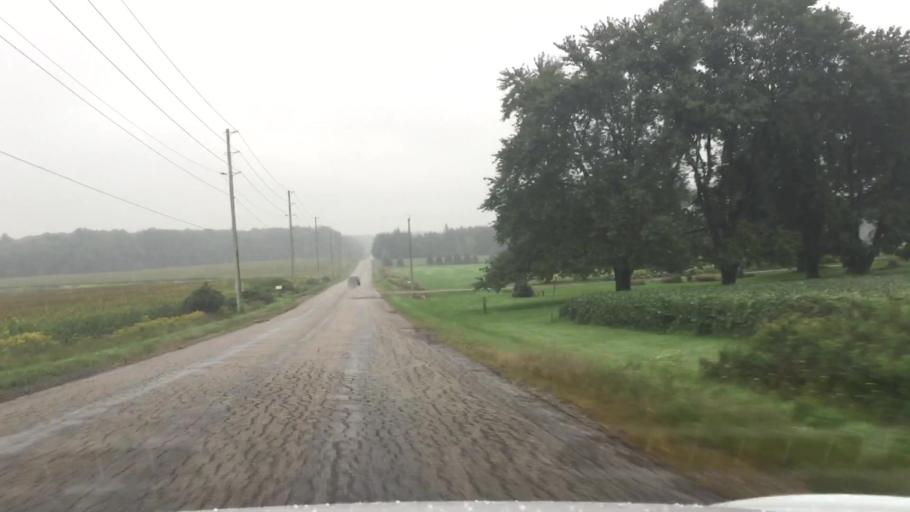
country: CA
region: Ontario
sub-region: Oxford County
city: Woodstock
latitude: 43.1110
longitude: -80.7161
